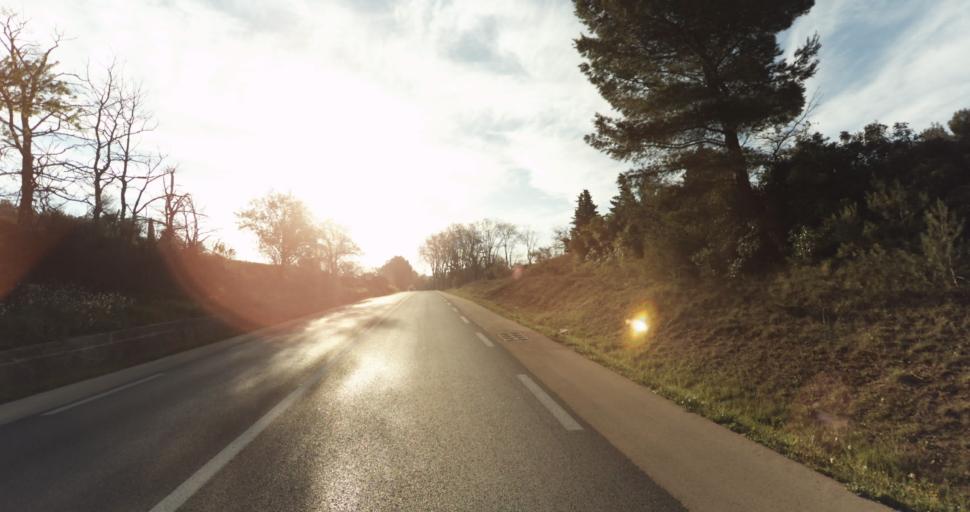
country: FR
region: Provence-Alpes-Cote d'Azur
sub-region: Departement des Bouches-du-Rhone
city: Eguilles
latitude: 43.5367
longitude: 5.3867
